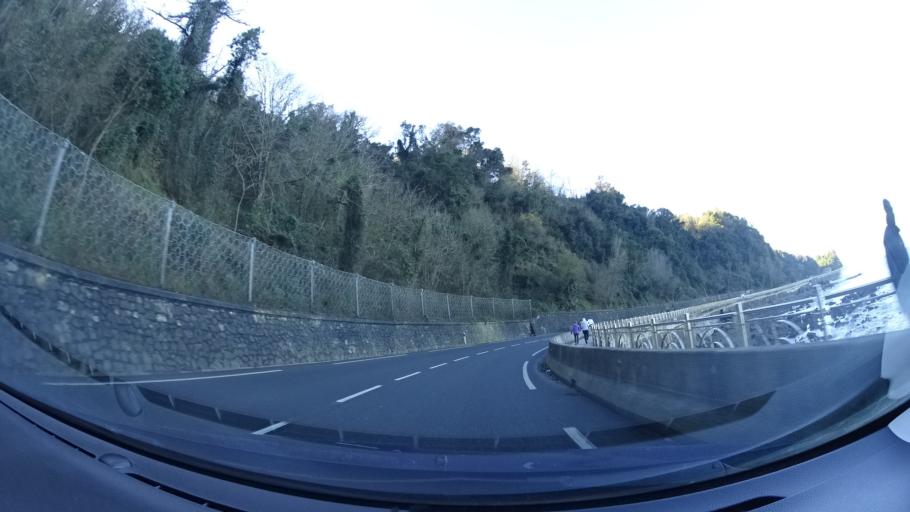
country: ES
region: Basque Country
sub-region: Provincia de Guipuzcoa
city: Getaria
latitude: 43.2940
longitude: -2.1890
